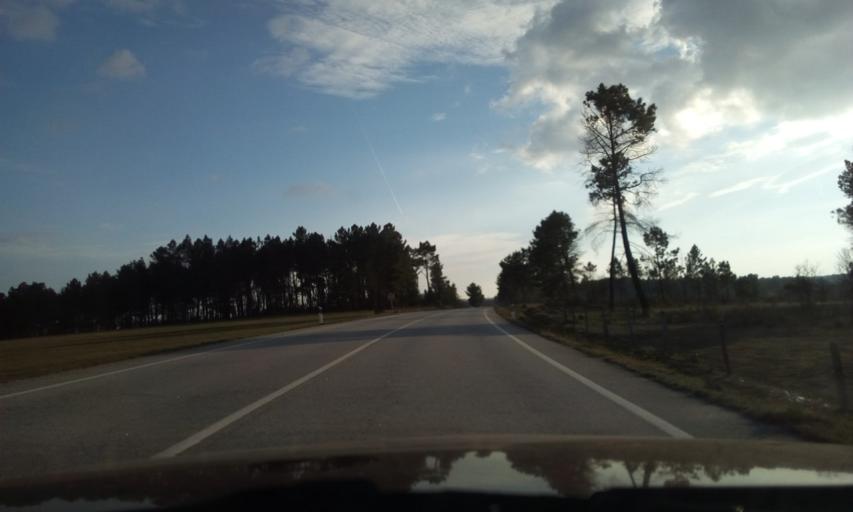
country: PT
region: Guarda
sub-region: Pinhel
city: Pinhel
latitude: 40.6433
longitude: -6.9689
